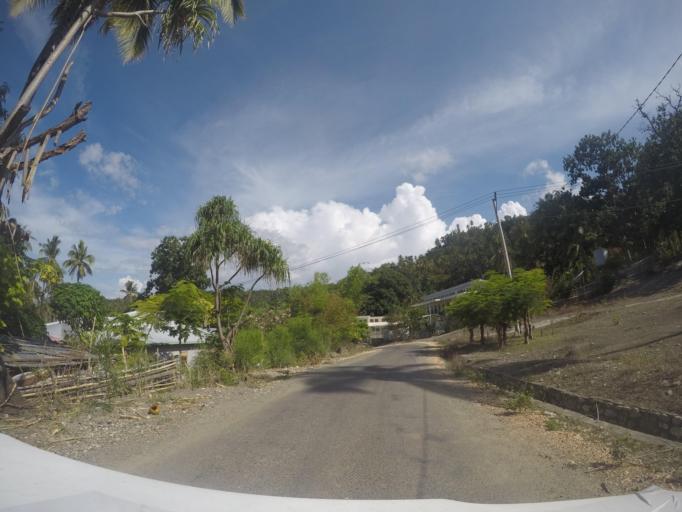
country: TL
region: Baucau
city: Baucau
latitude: -8.4572
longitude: 126.4582
